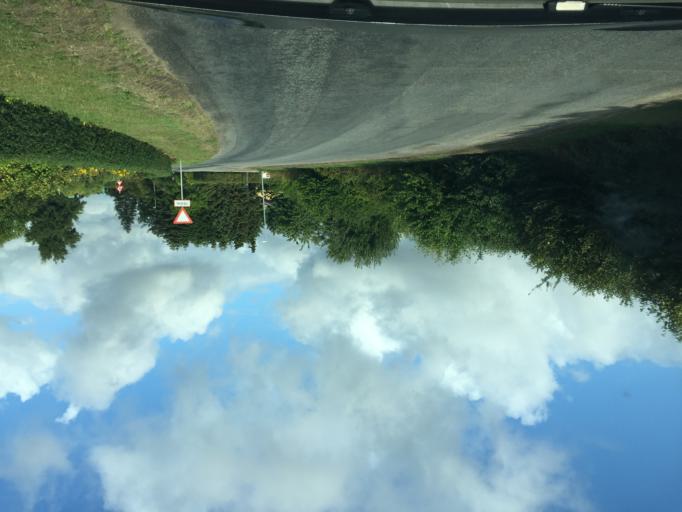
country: DK
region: South Denmark
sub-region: Faaborg-Midtfyn Kommune
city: Faaborg
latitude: 55.1957
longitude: 10.2510
